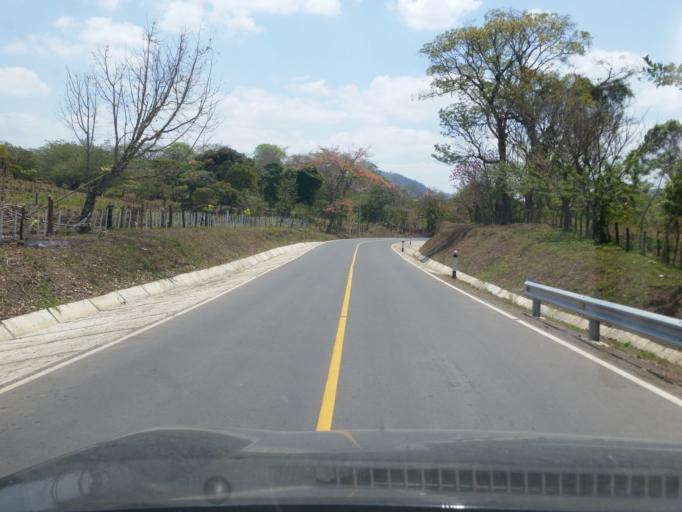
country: NI
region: Boaco
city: Boaco
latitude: 12.5921
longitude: -85.5365
